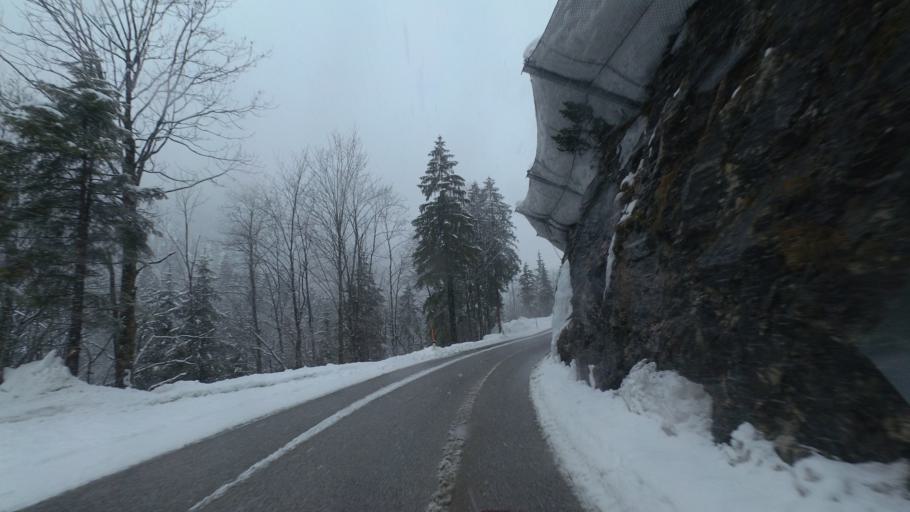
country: AT
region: Tyrol
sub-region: Politischer Bezirk Kitzbuhel
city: Kossen
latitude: 47.6812
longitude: 12.3958
